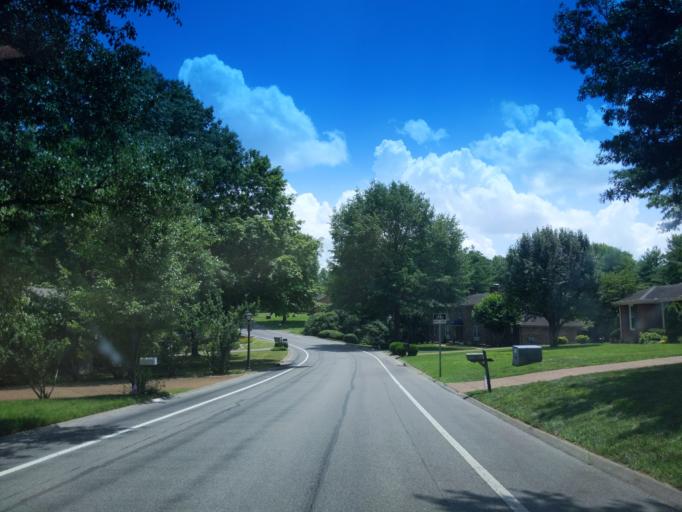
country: US
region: Tennessee
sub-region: Williamson County
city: Brentwood
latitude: 36.0437
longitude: -86.7622
